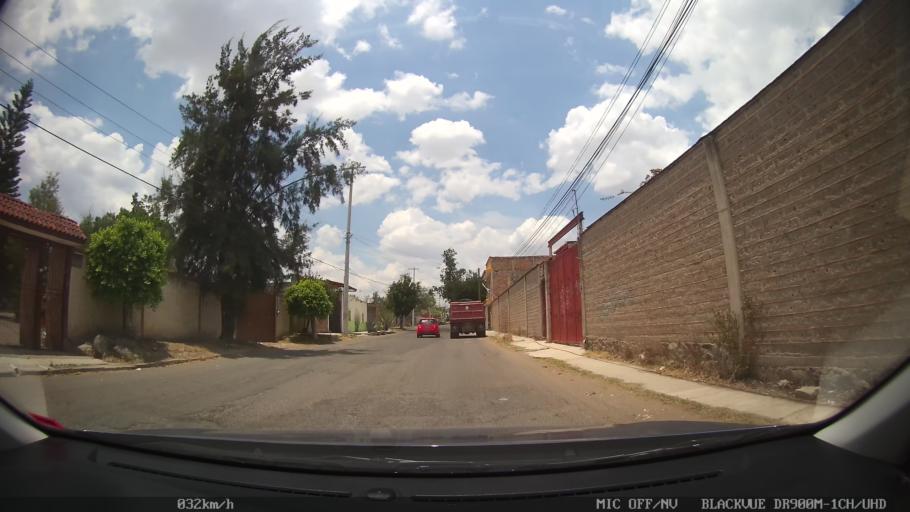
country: MX
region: Jalisco
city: Tonala
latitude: 20.6568
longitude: -103.2263
